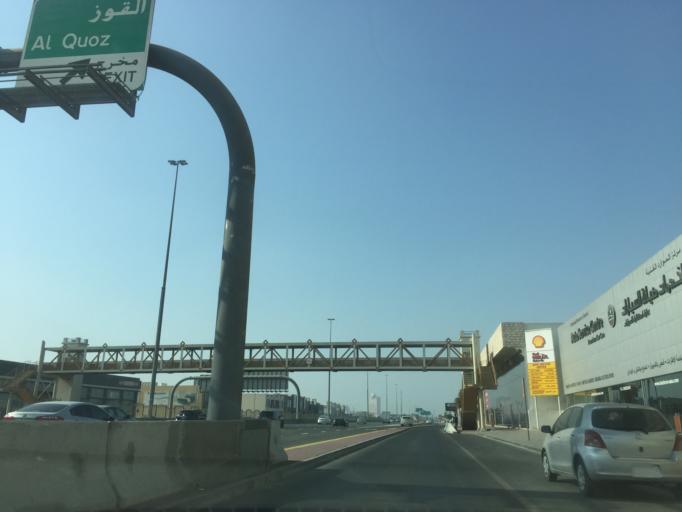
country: AE
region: Dubai
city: Dubai
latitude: 25.1066
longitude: 55.2271
